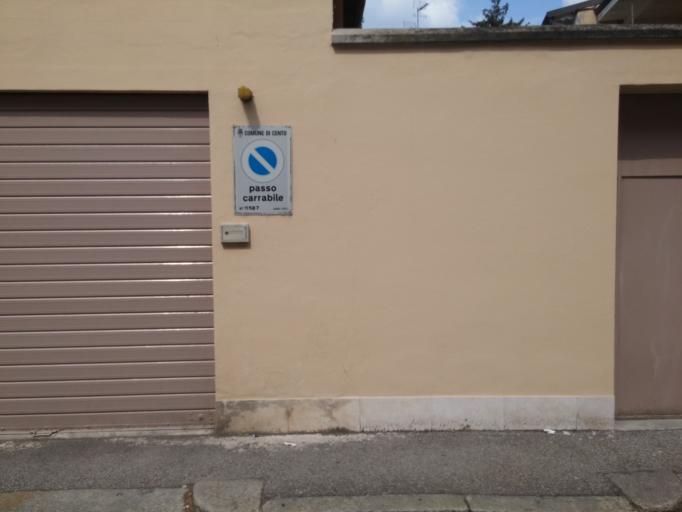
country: IT
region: Emilia-Romagna
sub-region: Provincia di Ferrara
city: Cento
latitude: 44.7266
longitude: 11.2852
